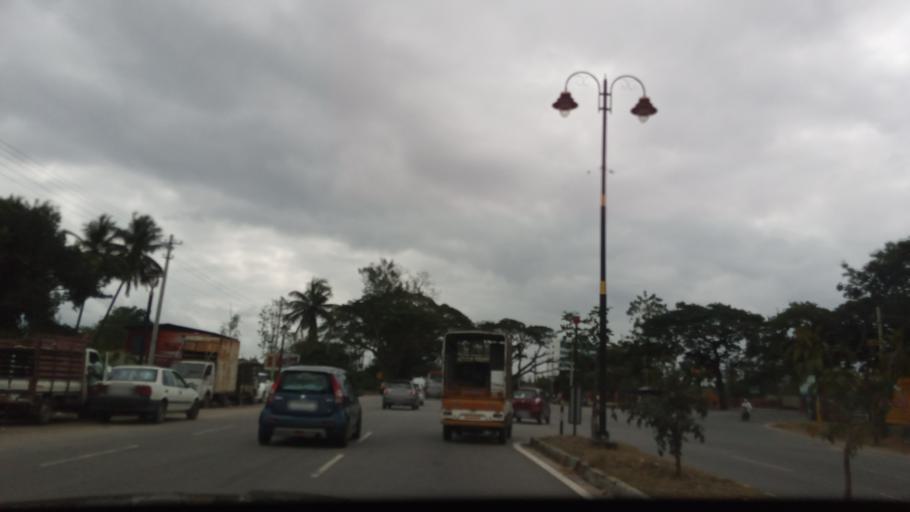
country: IN
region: Karnataka
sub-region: Mysore
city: Mysore
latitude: 12.3482
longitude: 76.6603
